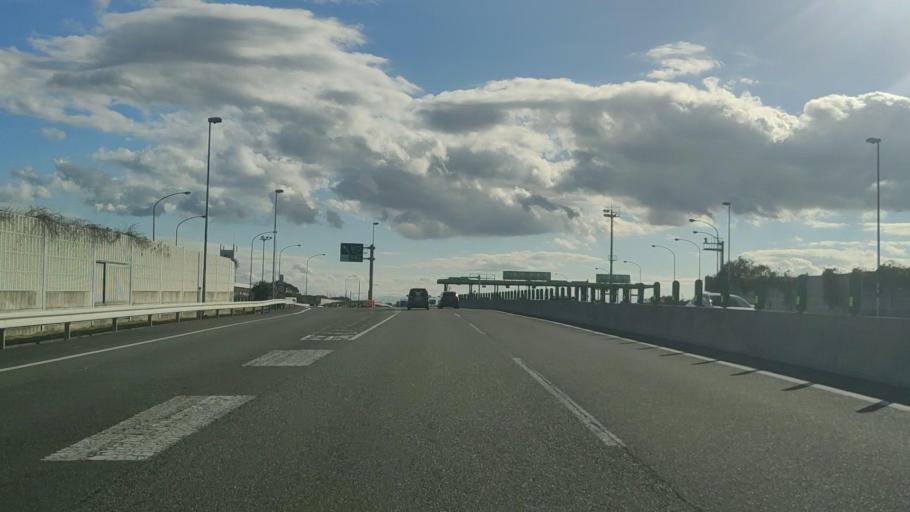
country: JP
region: Fukuoka
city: Nakama
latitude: 33.7973
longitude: 130.7435
